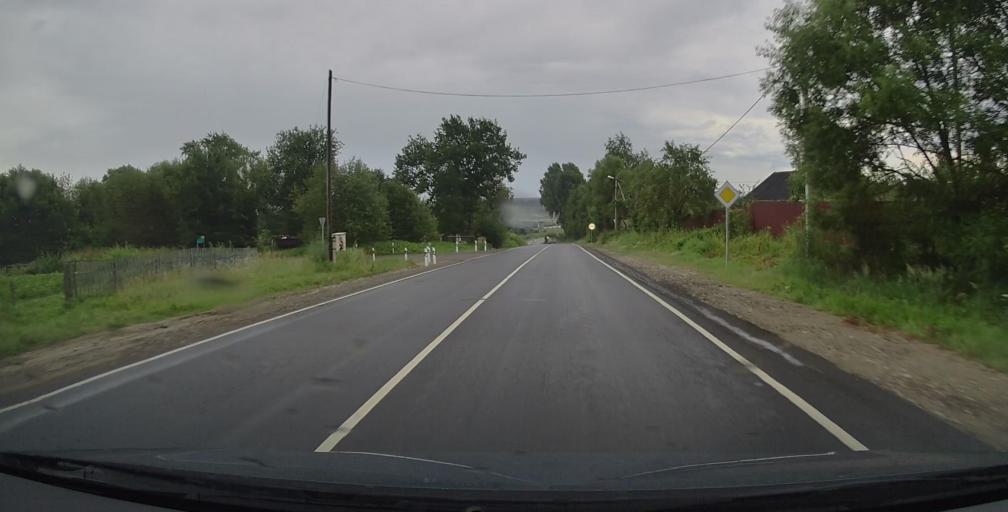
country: RU
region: Jaroslavl
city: Uglich
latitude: 57.5515
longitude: 38.2811
